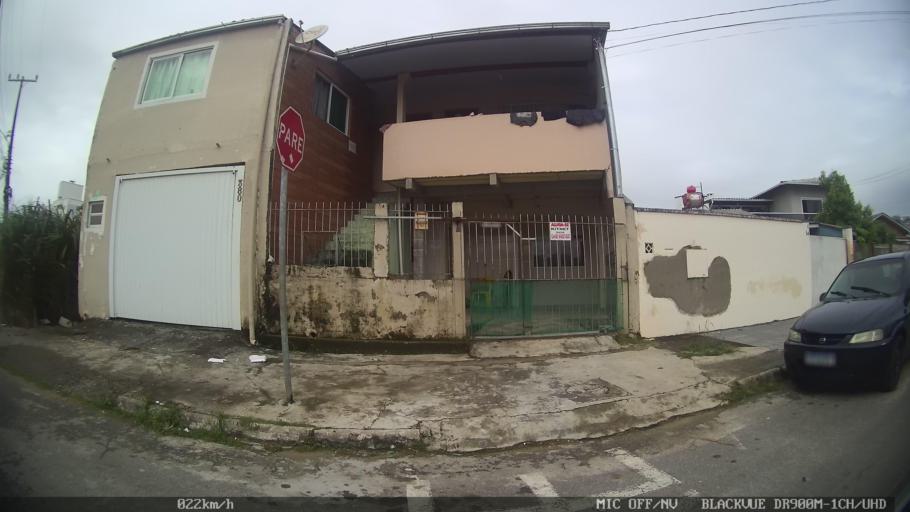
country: BR
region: Santa Catarina
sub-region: Biguacu
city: Biguacu
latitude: -27.5382
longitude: -48.6394
